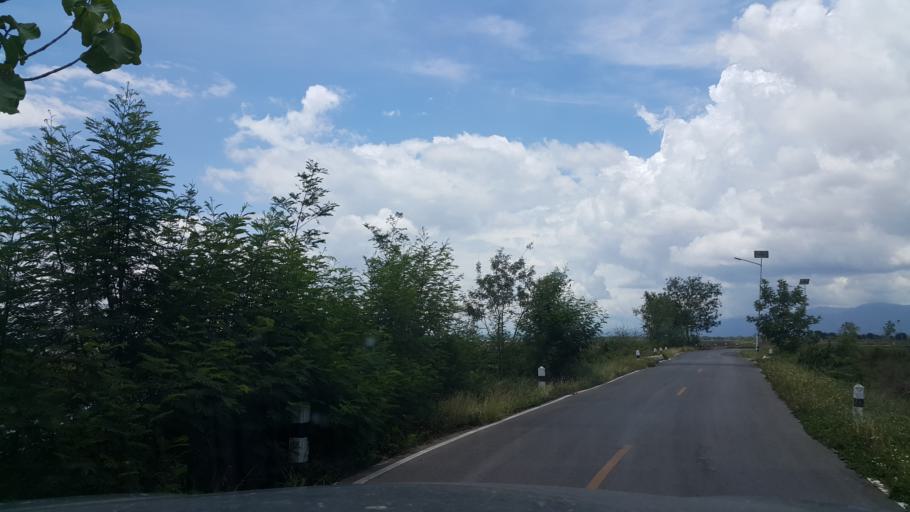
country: TH
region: Phayao
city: Phayao
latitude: 19.1836
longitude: 99.8548
